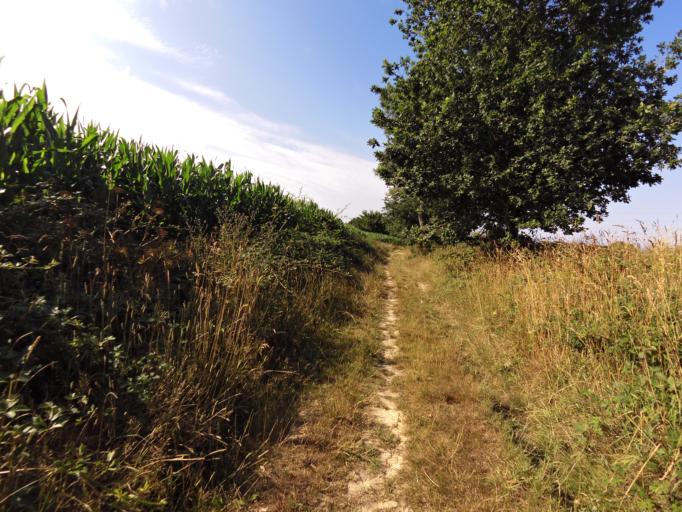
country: FR
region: Brittany
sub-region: Departement d'Ille-et-Vilaine
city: Chanteloup
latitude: 47.9319
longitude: -1.6289
